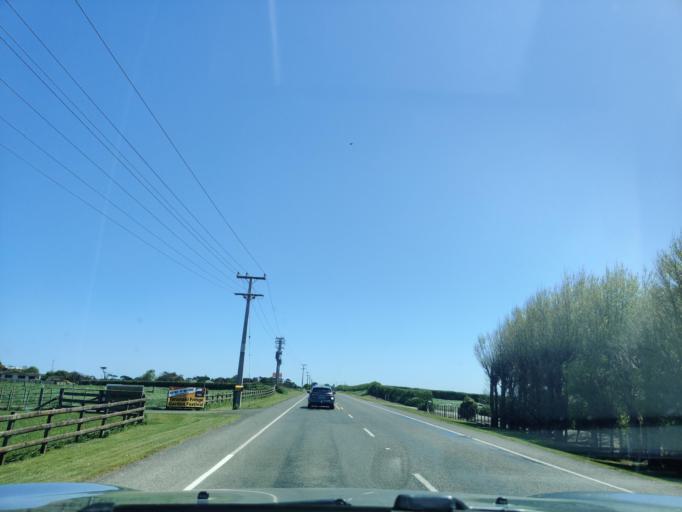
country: NZ
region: Taranaki
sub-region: South Taranaki District
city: Hawera
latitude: -39.6057
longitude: 174.3152
